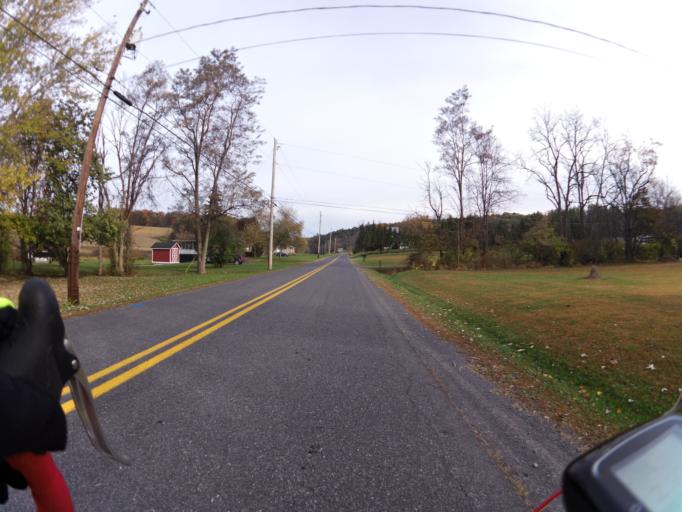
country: US
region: Pennsylvania
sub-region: Union County
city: New Columbia
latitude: 41.0295
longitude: -76.9217
